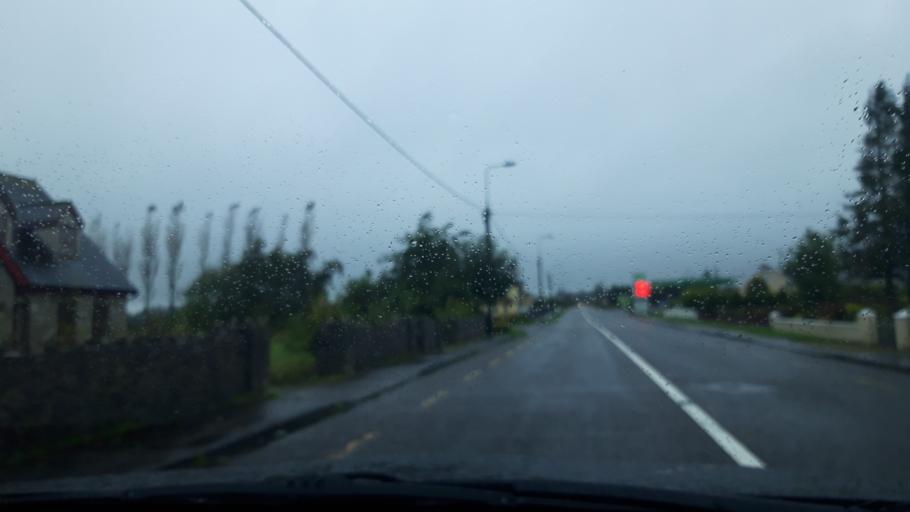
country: IE
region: Connaught
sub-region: Roscommon
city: Ballaghaderreen
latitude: 53.9056
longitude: -8.5875
